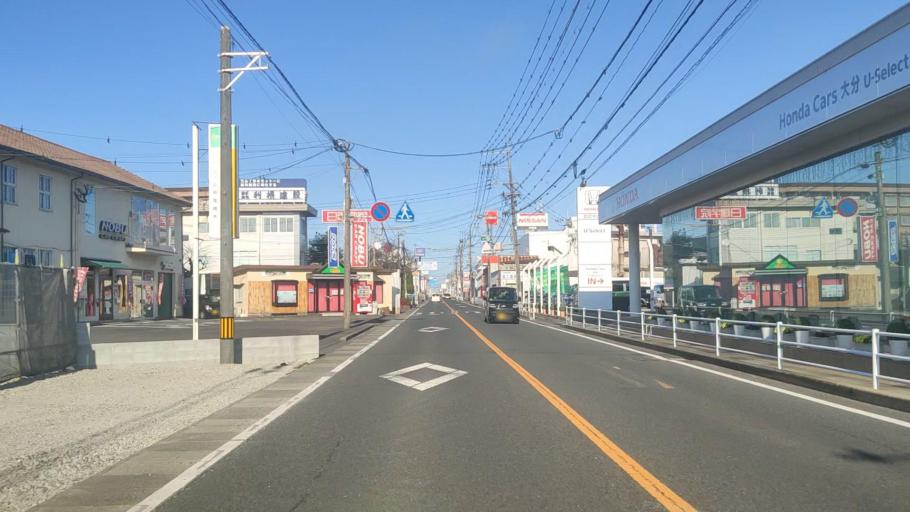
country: JP
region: Oita
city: Oita
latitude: 33.2135
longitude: 131.6099
